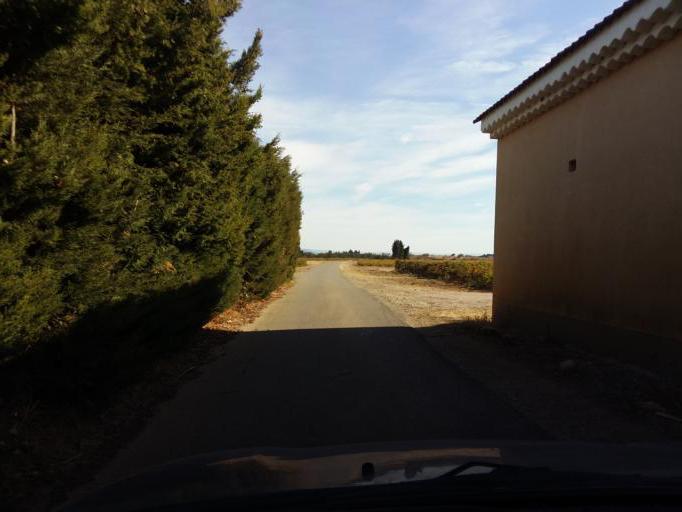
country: FR
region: Provence-Alpes-Cote d'Azur
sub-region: Departement du Vaucluse
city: Piolenc
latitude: 44.1780
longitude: 4.7878
